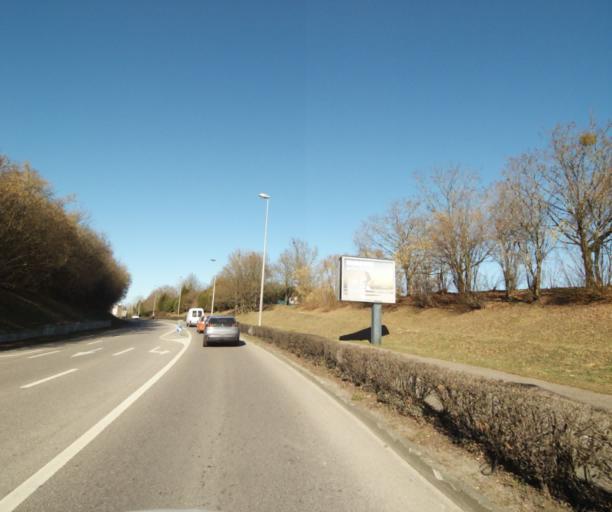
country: FR
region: Lorraine
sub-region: Departement de Meurthe-et-Moselle
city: Vandoeuvre-les-Nancy
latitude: 48.6552
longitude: 6.1791
